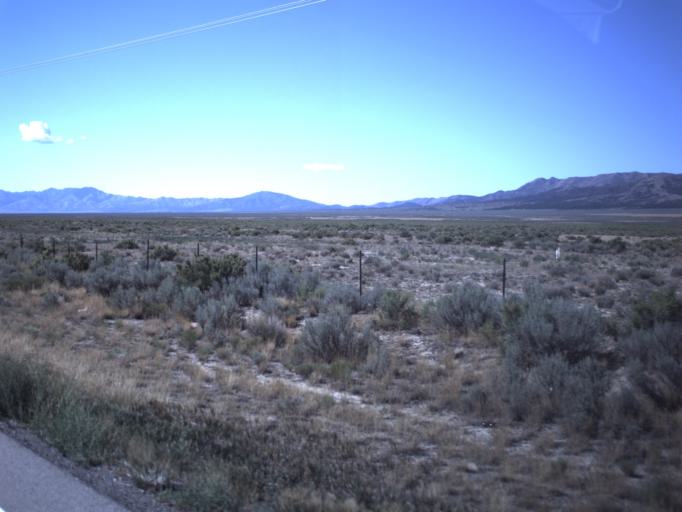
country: US
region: Utah
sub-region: Tooele County
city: Tooele
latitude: 40.2672
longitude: -112.3974
